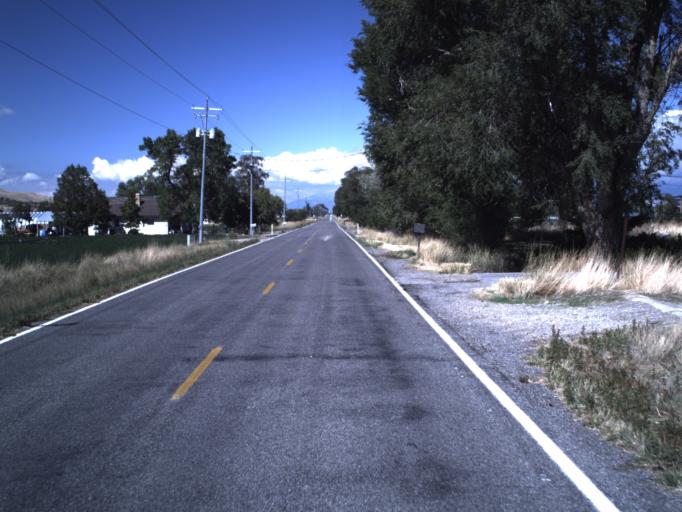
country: US
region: Utah
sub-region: Utah County
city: West Mountain
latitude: 40.0649
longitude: -111.7876
